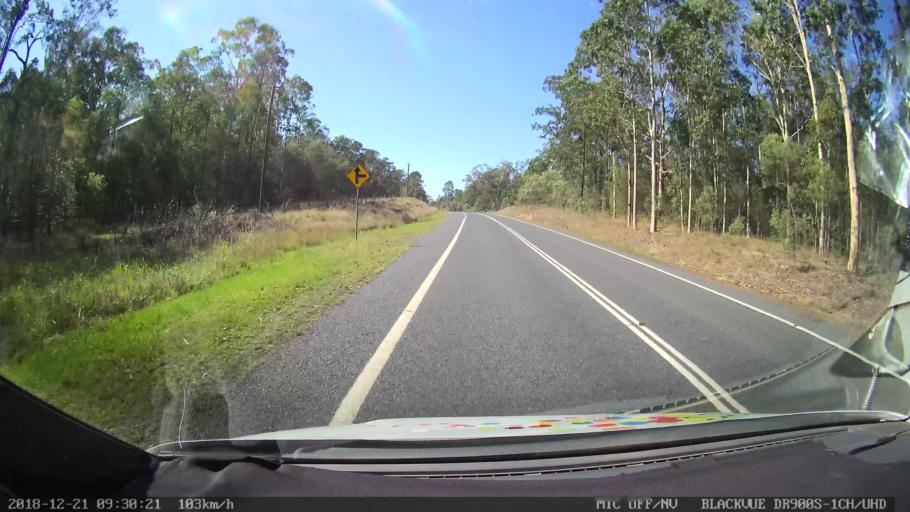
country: AU
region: New South Wales
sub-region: Clarence Valley
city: Maclean
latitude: -29.4452
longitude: 152.9919
